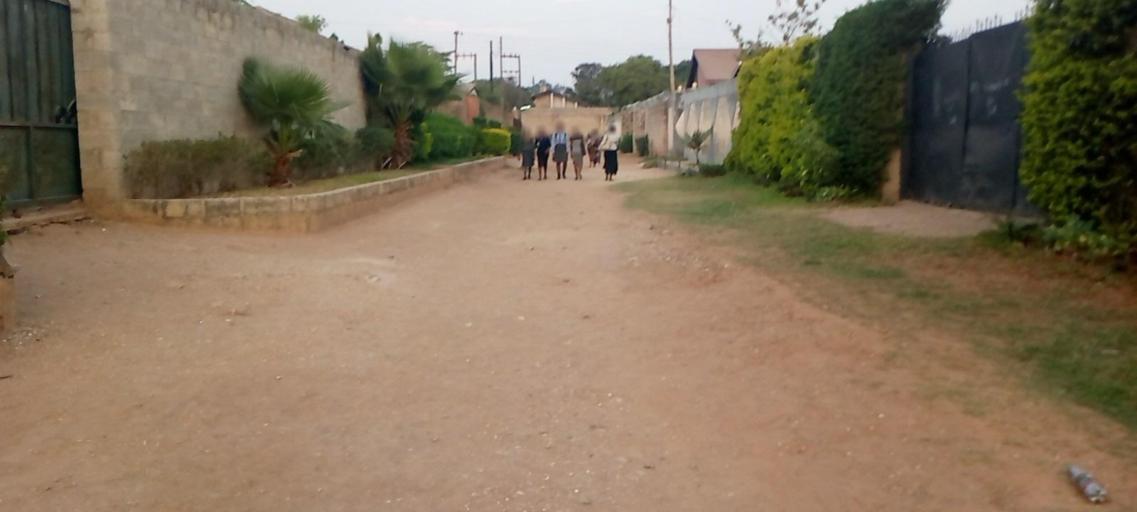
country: ZM
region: Lusaka
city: Lusaka
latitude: -15.4064
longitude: 28.3483
